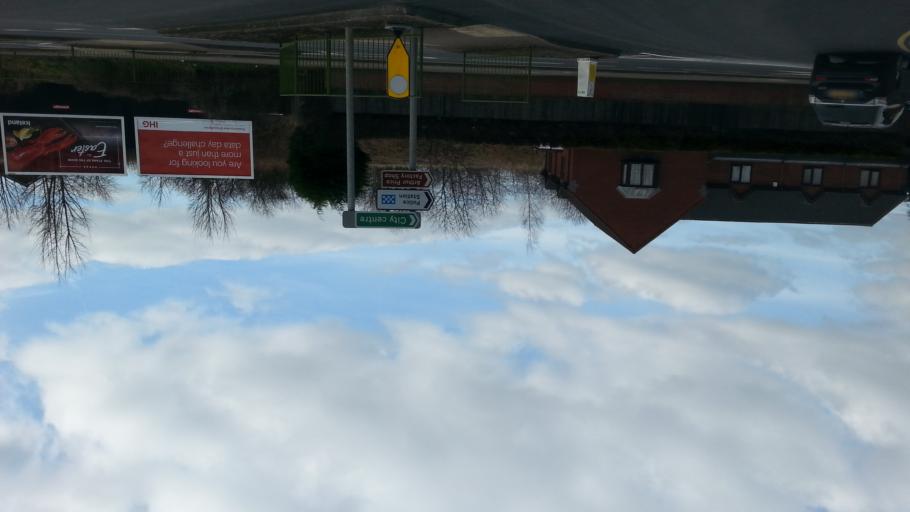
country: GB
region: England
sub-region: Staffordshire
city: Lichfield
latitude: 52.6761
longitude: -1.8315
